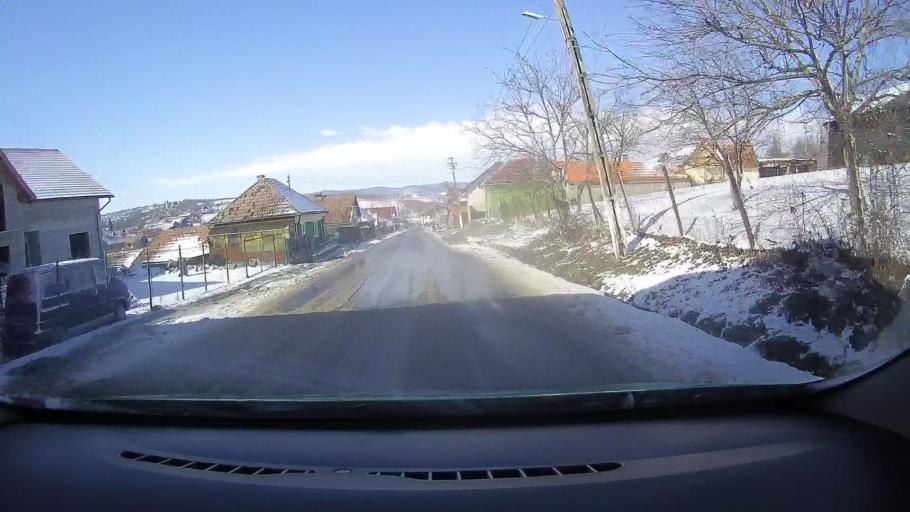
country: RO
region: Sibiu
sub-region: Comuna Rosia
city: Rosia
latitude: 45.8023
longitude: 24.2916
